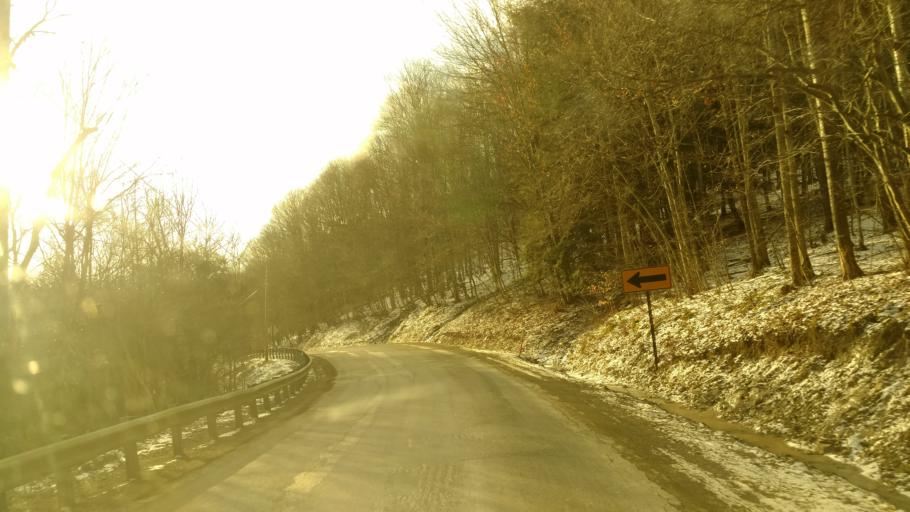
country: US
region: New York
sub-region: Allegany County
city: Andover
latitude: 41.9459
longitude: -77.8236
